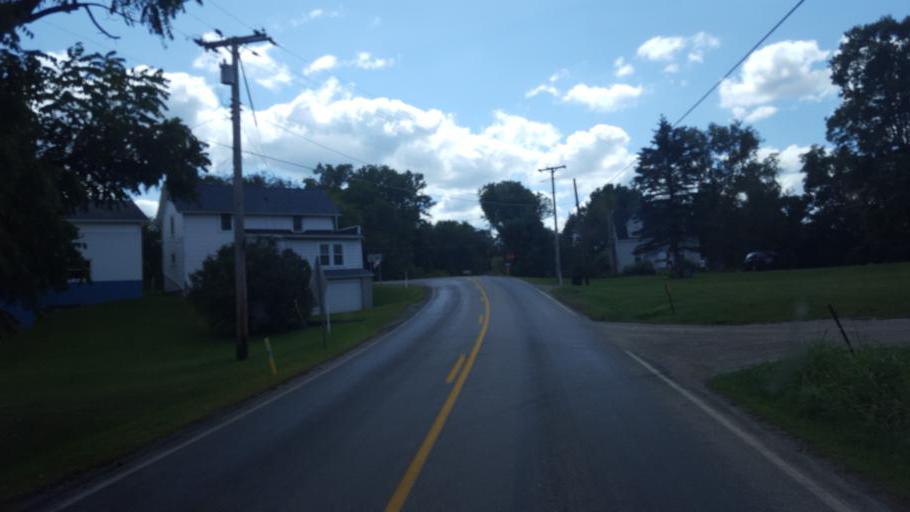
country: US
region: Ohio
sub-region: Ashland County
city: Ashland
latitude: 40.9262
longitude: -82.2817
